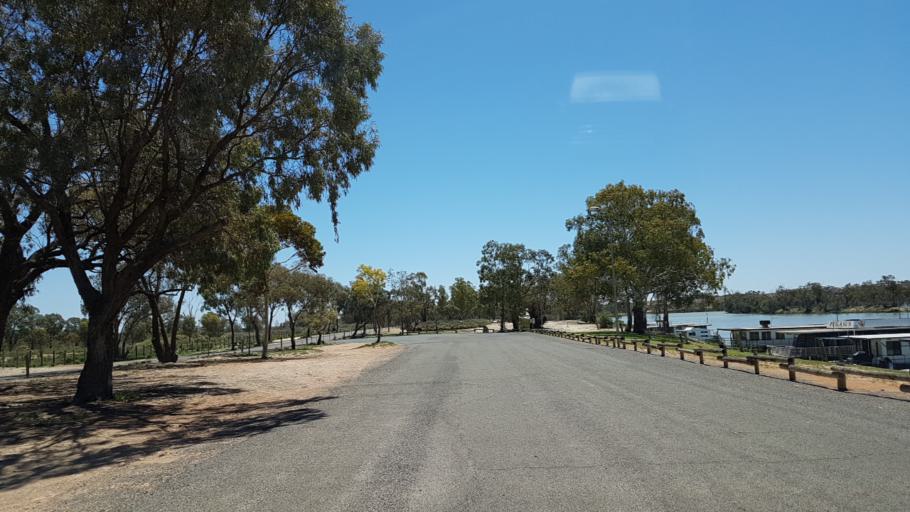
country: AU
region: South Australia
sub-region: Loxton Waikerie
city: Waikerie
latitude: -34.1712
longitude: 139.9794
